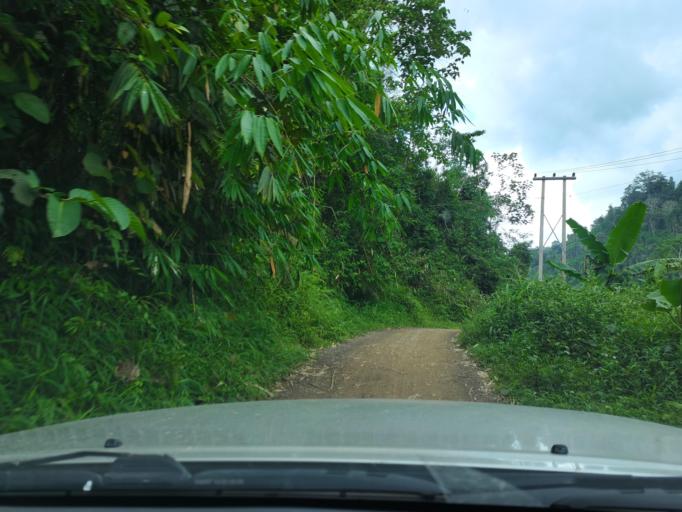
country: LA
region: Loungnamtha
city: Muang Long
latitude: 20.7666
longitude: 101.0180
